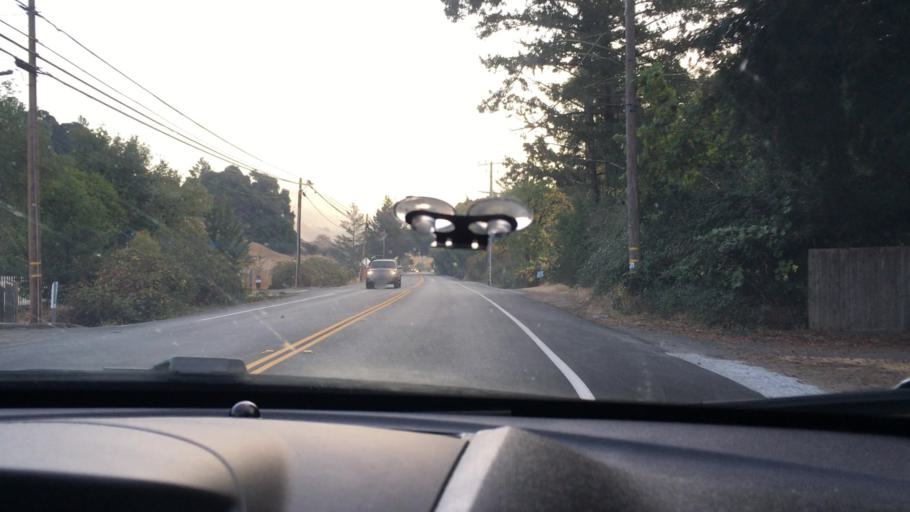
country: US
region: California
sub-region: Marin County
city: Lagunitas-Forest Knolls
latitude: 38.0157
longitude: -122.6846
